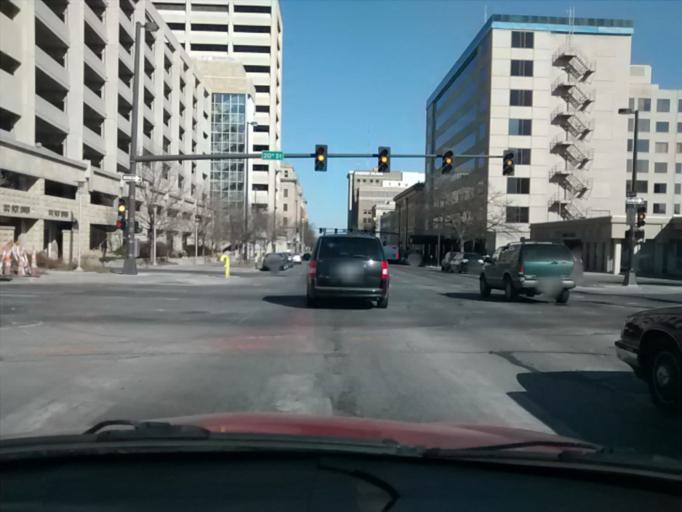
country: US
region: Nebraska
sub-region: Douglas County
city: Omaha
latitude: 41.2566
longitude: -95.9425
